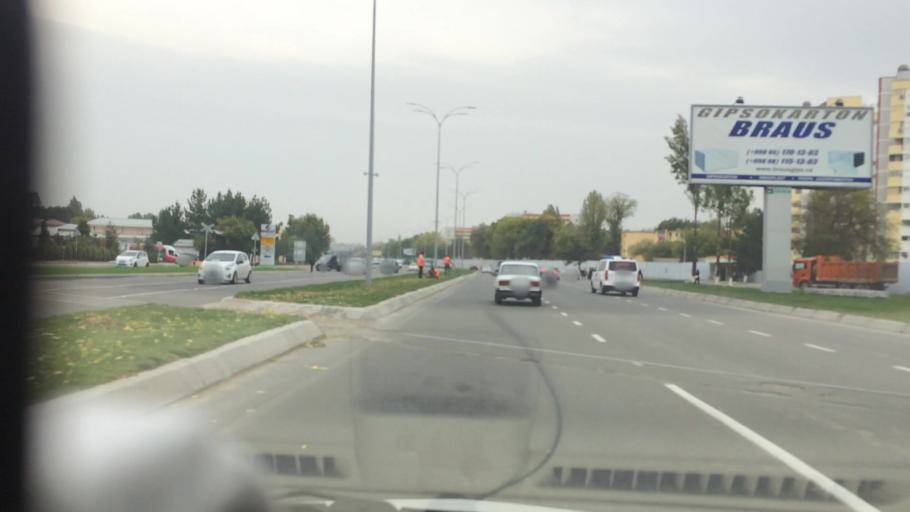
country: UZ
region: Toshkent
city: Salor
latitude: 41.3022
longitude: 69.3439
